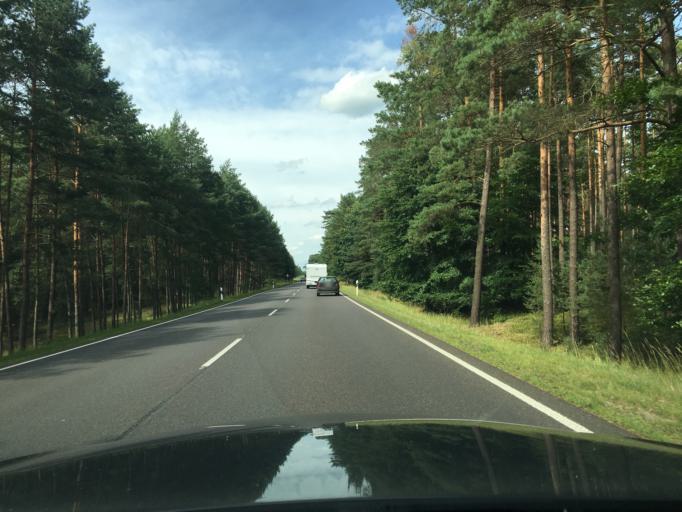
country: DE
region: Brandenburg
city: Furstenberg
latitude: 53.2705
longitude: 13.1145
